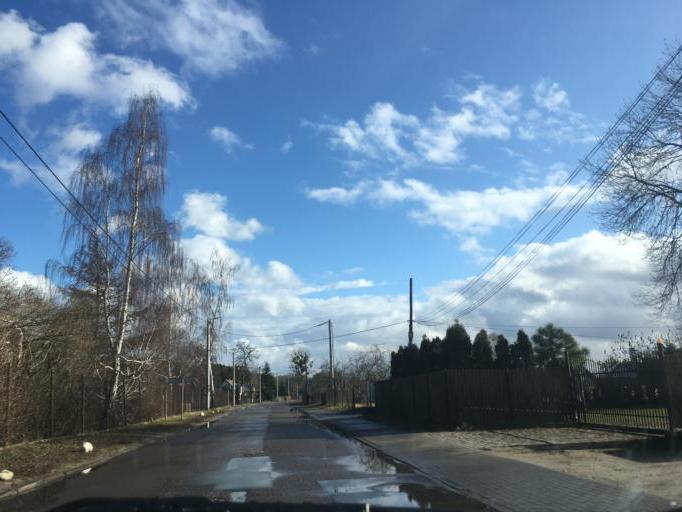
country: PL
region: Pomeranian Voivodeship
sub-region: Powiat gdanski
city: Cedry Wielkie
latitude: 54.3491
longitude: 18.8004
